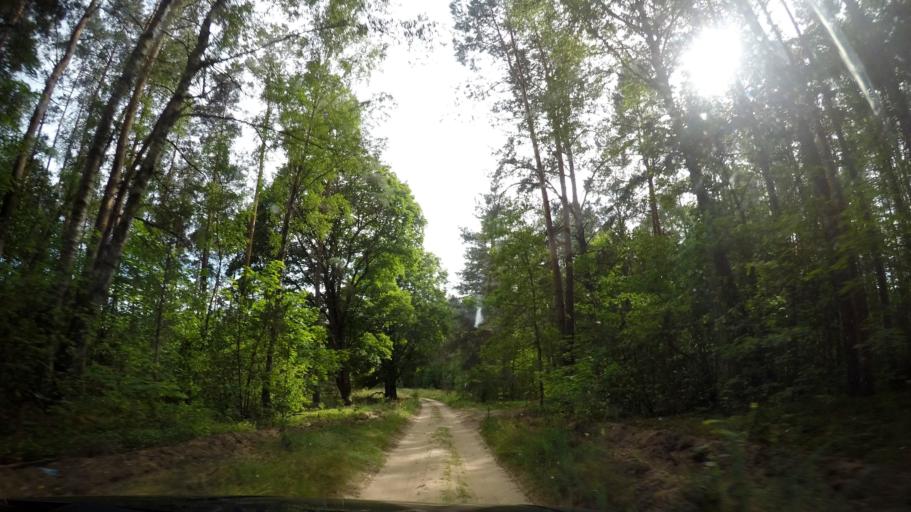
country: BY
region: Grodnenskaya
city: Skidal'
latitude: 53.8255
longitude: 24.1789
